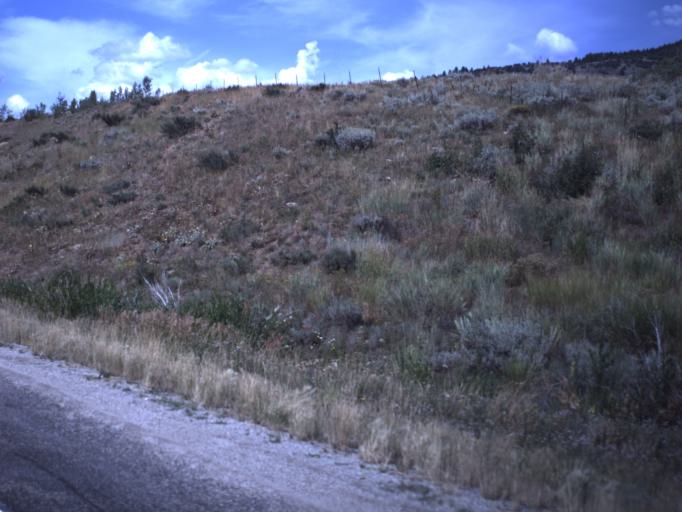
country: US
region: Utah
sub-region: Cache County
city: Richmond
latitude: 41.9139
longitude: -111.5625
